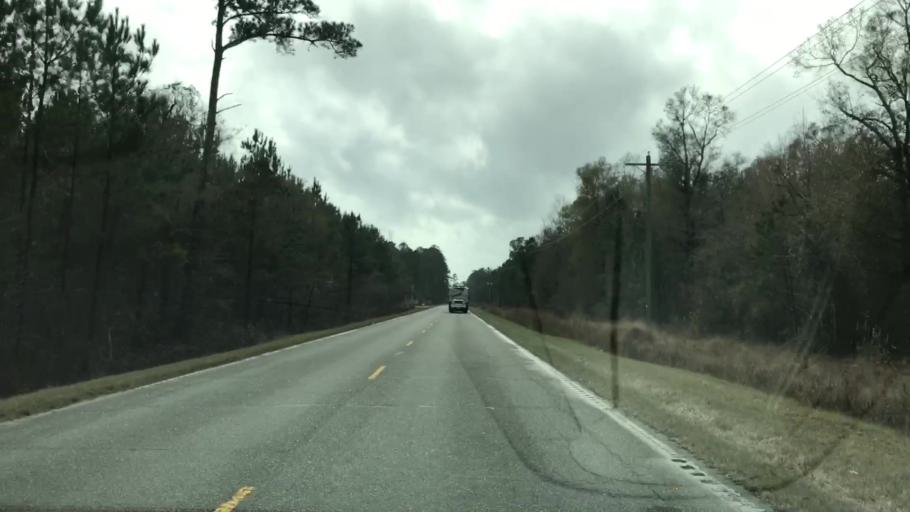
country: US
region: South Carolina
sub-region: Georgetown County
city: Murrells Inlet
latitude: 33.6271
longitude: -79.1901
